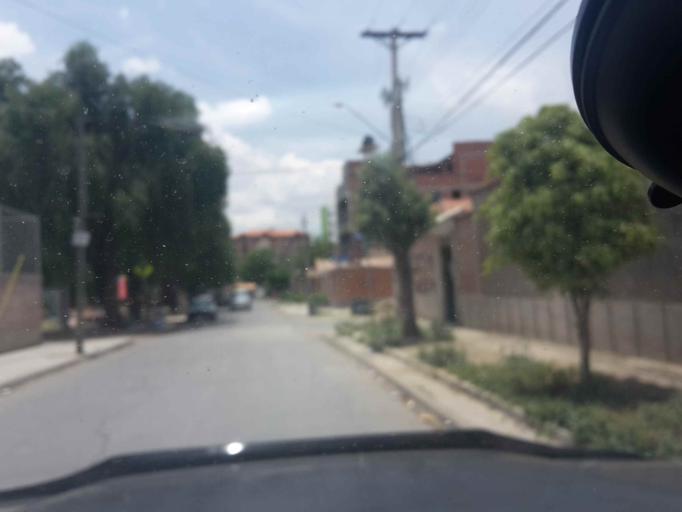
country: BO
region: Cochabamba
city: Cochabamba
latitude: -17.3760
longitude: -66.1867
